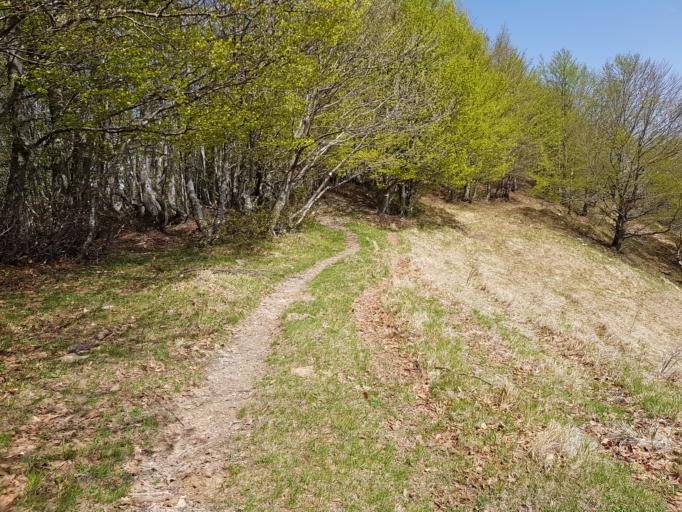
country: IT
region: Liguria
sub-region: Provincia di Genova
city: Fascia
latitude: 44.6231
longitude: 9.2450
